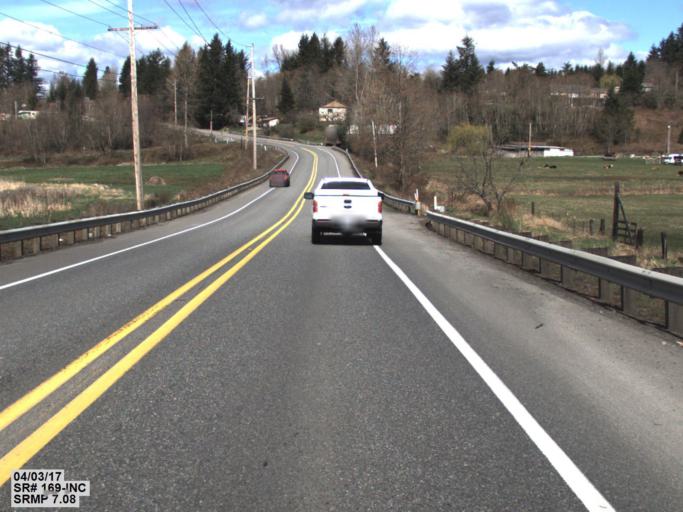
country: US
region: Washington
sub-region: King County
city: Black Diamond
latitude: 47.3011
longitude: -121.9998
